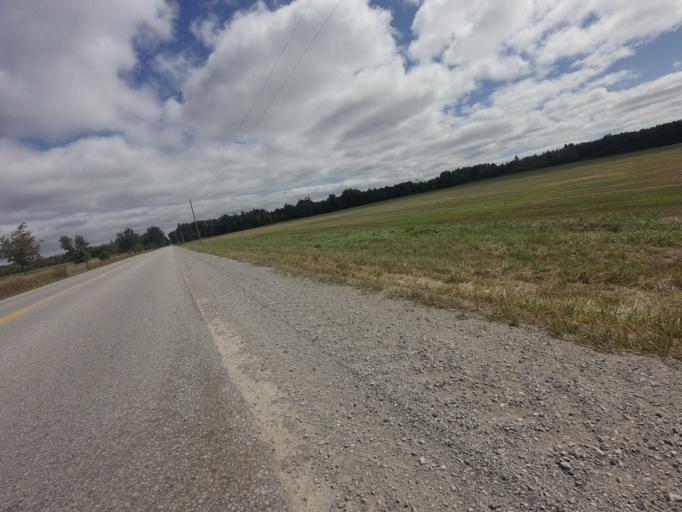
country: CA
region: Ontario
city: Uxbridge
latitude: 44.1218
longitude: -79.1833
